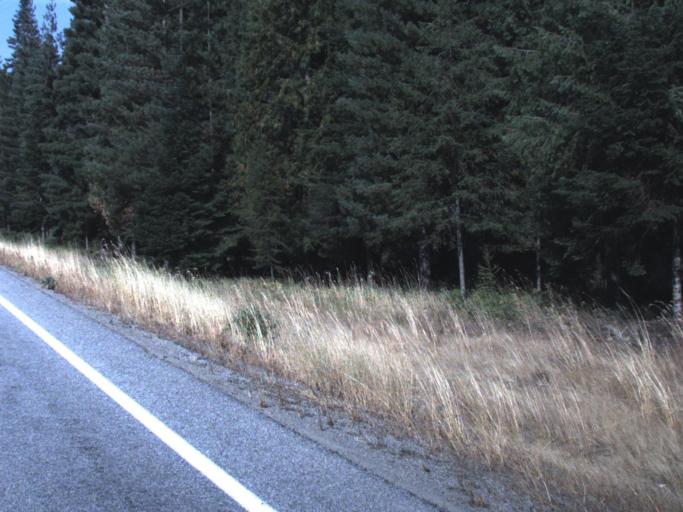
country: US
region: Washington
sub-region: Pend Oreille County
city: Newport
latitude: 48.2749
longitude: -117.2846
